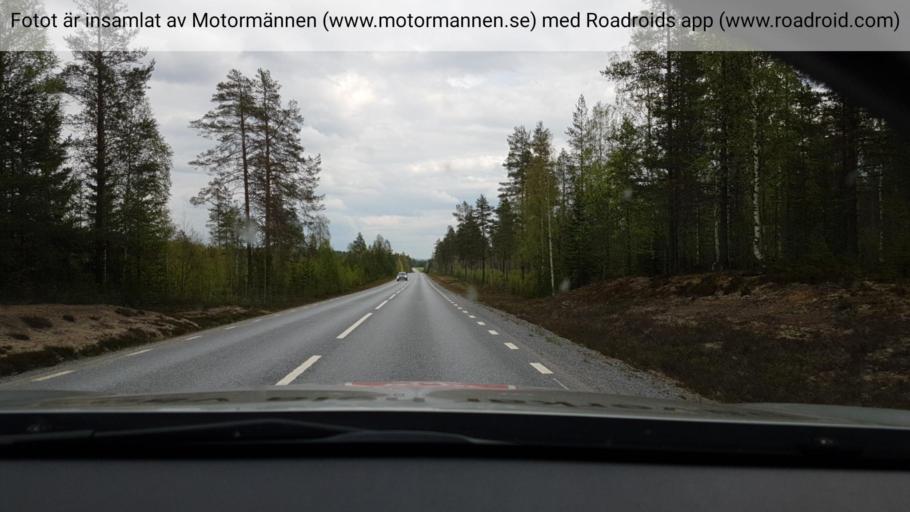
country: SE
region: Vaesterbotten
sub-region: Bjurholms Kommun
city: Bjurholm
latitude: 63.9295
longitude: 19.0025
